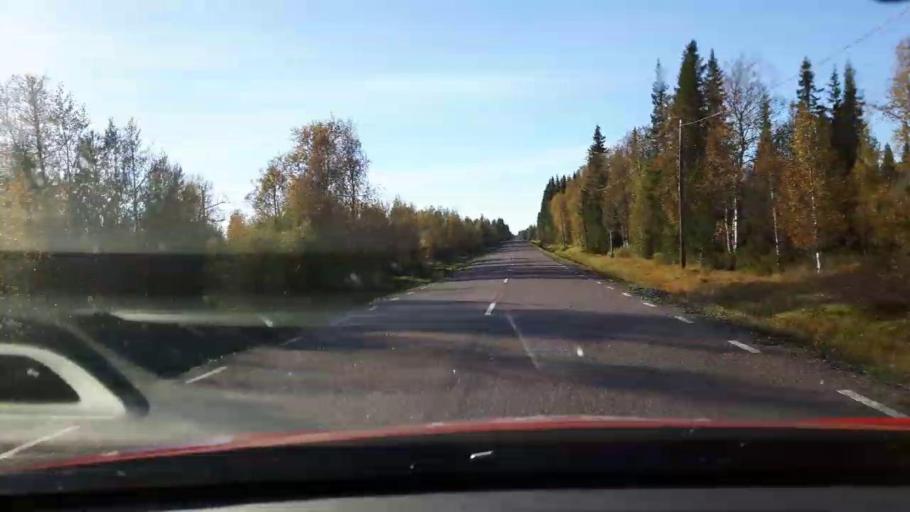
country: SE
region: Jaemtland
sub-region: Stroemsunds Kommun
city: Stroemsund
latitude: 63.8586
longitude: 15.1962
